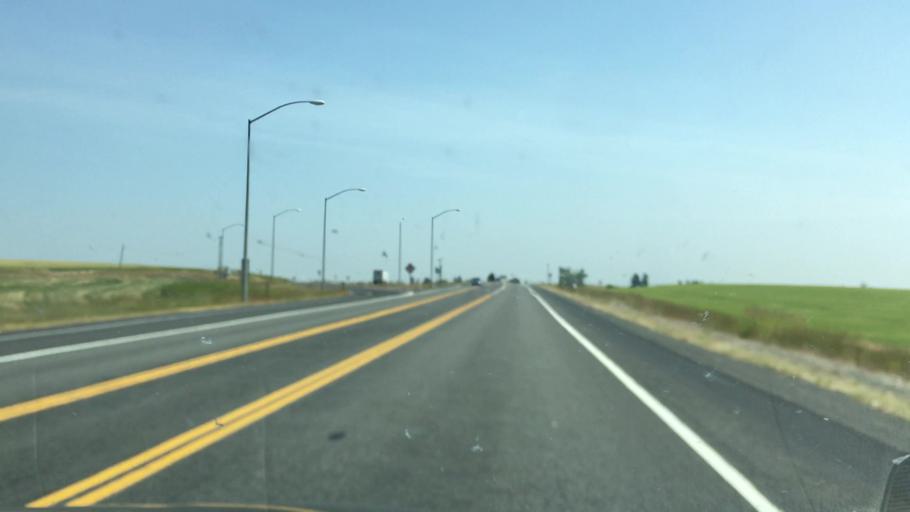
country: US
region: Idaho
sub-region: Lewis County
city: Nezperce
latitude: 46.2363
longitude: -116.4918
